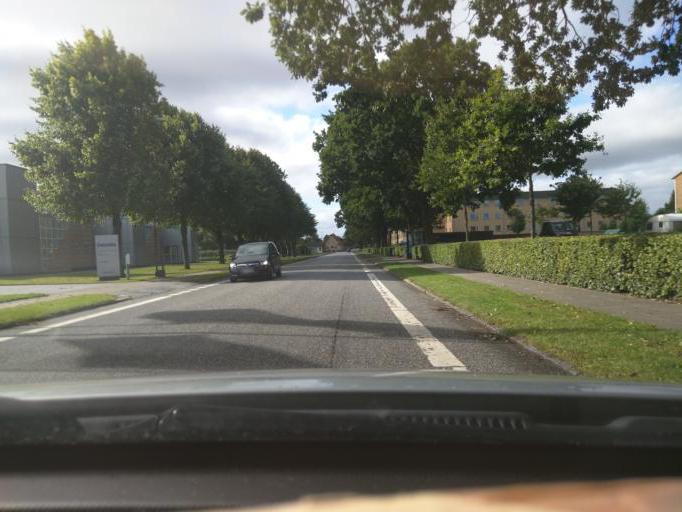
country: DK
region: Central Jutland
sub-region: Viborg Kommune
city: Viborg
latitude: 56.4594
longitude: 9.3934
